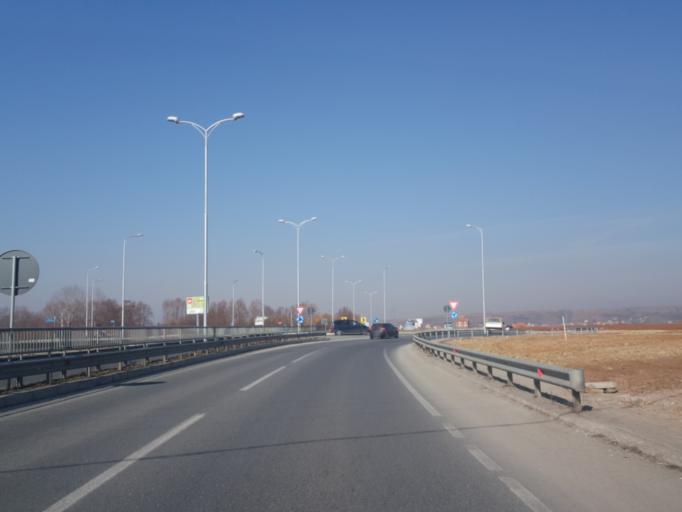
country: XK
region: Pristina
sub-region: Komuna e Obiliqit
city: Obiliq
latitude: 42.7252
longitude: 21.0803
